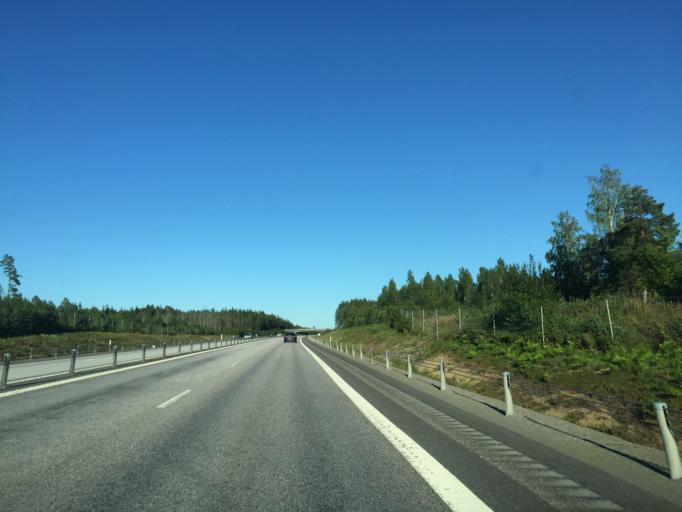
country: SE
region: OErebro
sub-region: Lekebergs Kommun
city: Fjugesta
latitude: 59.2535
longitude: 14.8675
